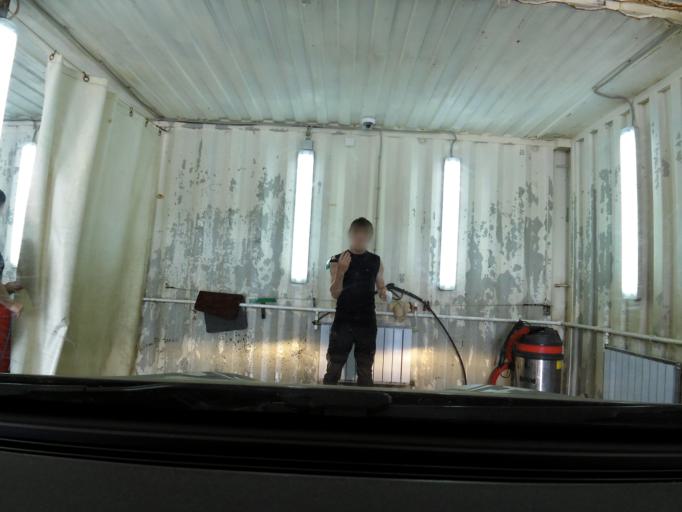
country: RU
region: Sverdlovsk
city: Shirokaya Rechka
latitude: 56.8011
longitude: 60.4930
